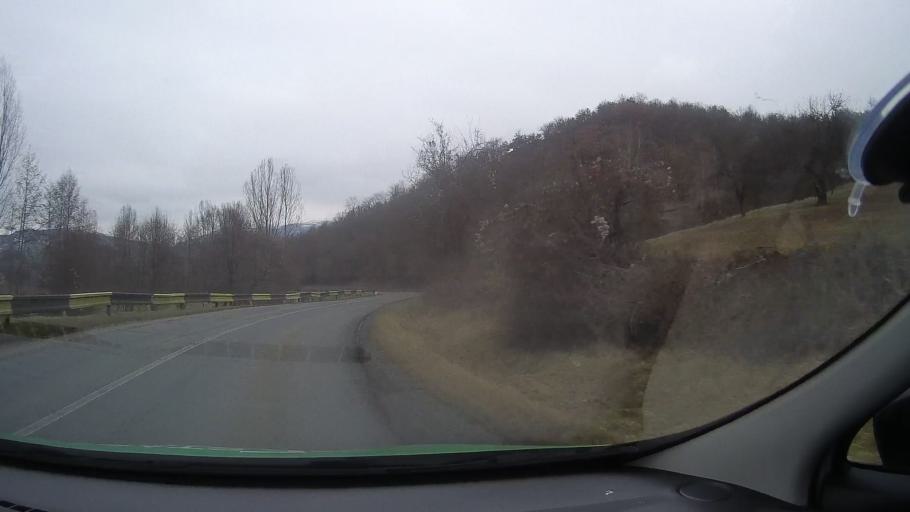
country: RO
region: Alba
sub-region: Comuna Metes
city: Metes
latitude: 46.1034
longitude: 23.4513
